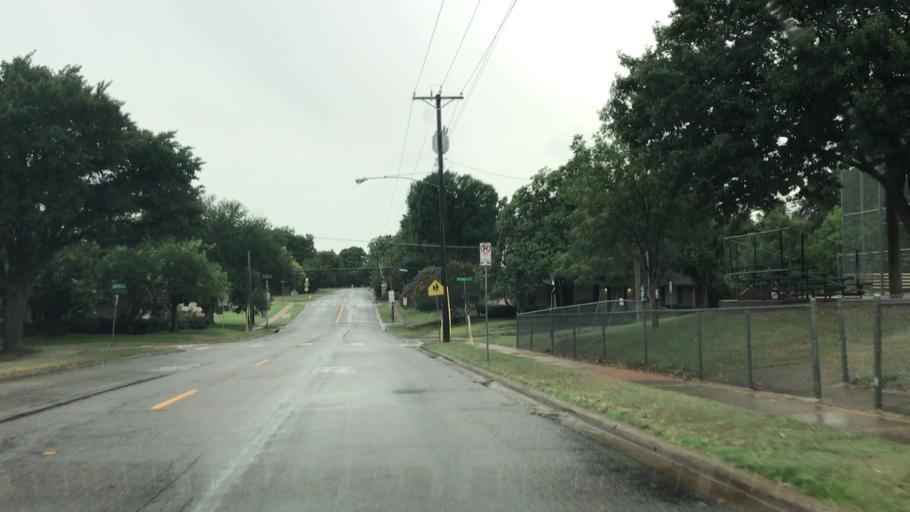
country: US
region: Texas
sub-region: Dallas County
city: Richardson
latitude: 32.9337
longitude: -96.7771
